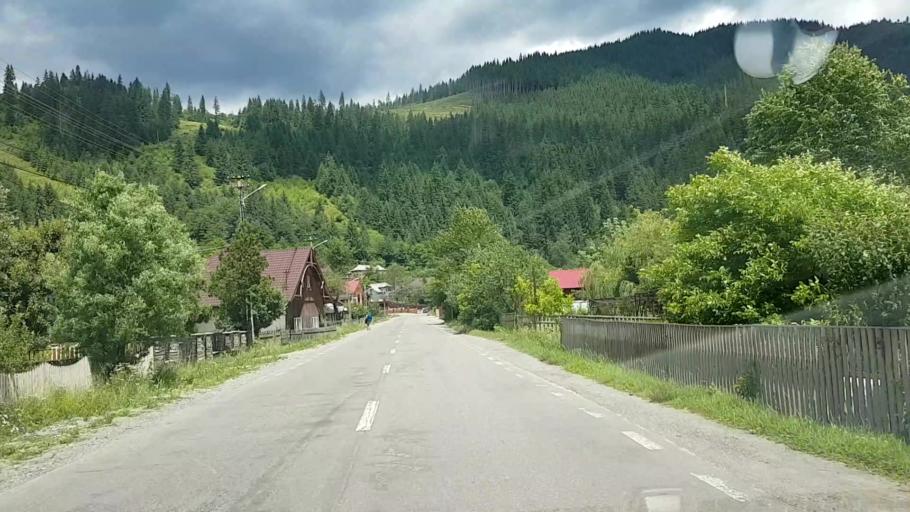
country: RO
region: Suceava
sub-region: Comuna Brosteni
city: Brosteni
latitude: 47.2414
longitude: 25.7009
